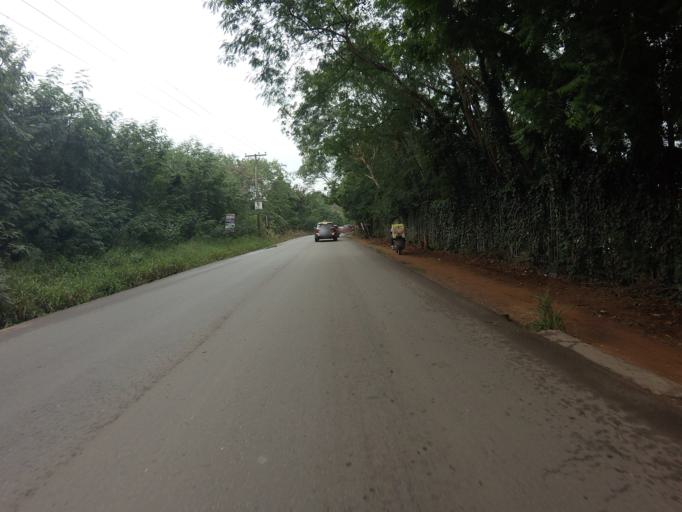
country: GH
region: Greater Accra
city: Dome
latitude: 5.6327
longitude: -0.2170
